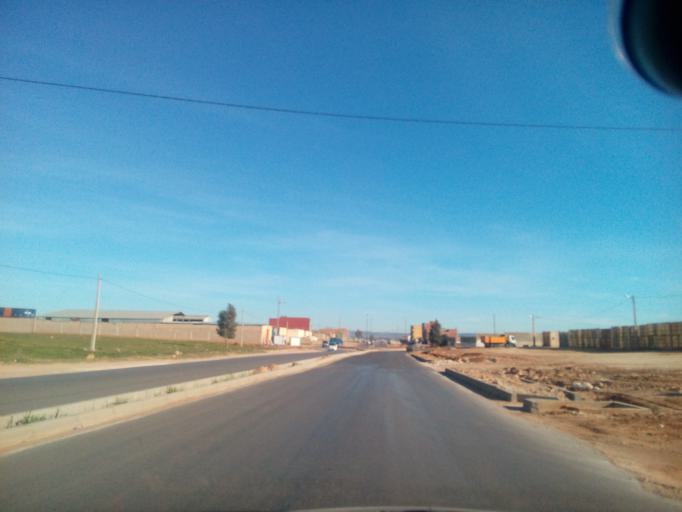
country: DZ
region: Mostaganem
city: Mostaganem
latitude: 35.9099
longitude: 0.1592
